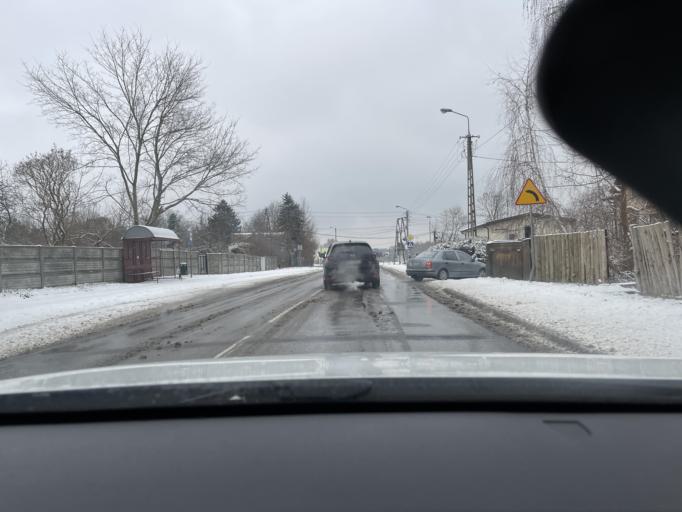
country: PL
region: Masovian Voivodeship
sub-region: Powiat zyrardowski
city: Zyrardow
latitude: 52.0310
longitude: 20.4648
